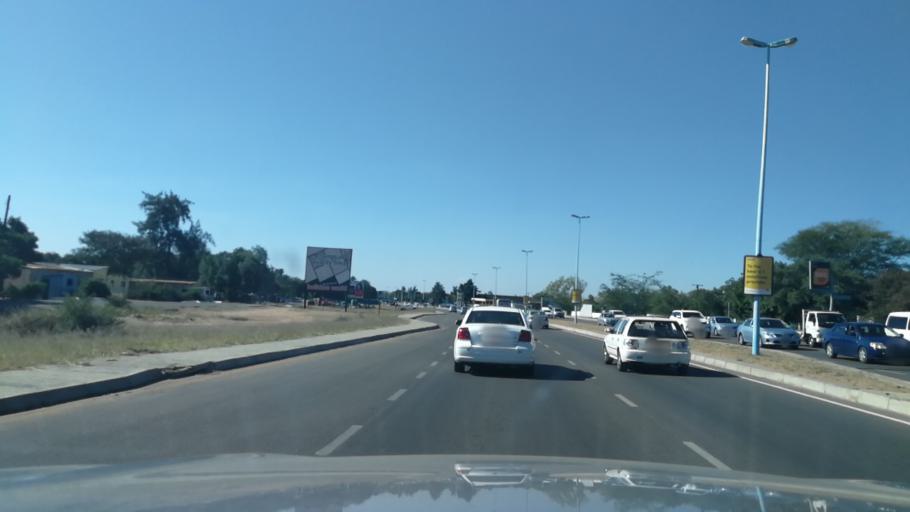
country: BW
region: South East
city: Gaborone
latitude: -24.6794
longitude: 25.9173
